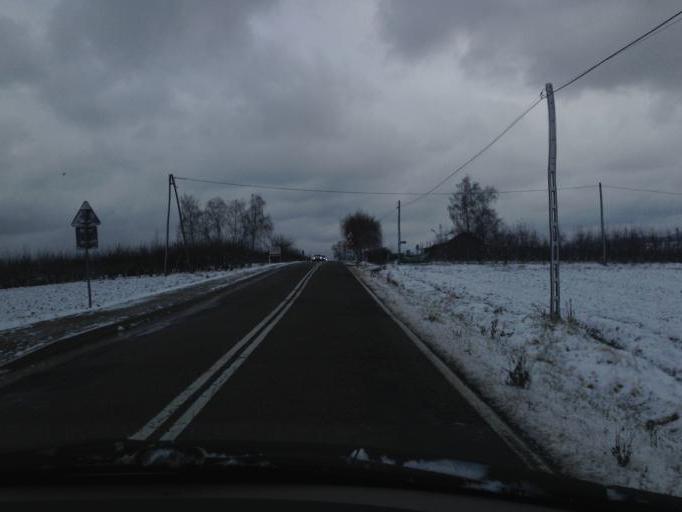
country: PL
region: Lesser Poland Voivodeship
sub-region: Powiat bochenski
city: Trzciana
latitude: 49.8639
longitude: 20.3685
